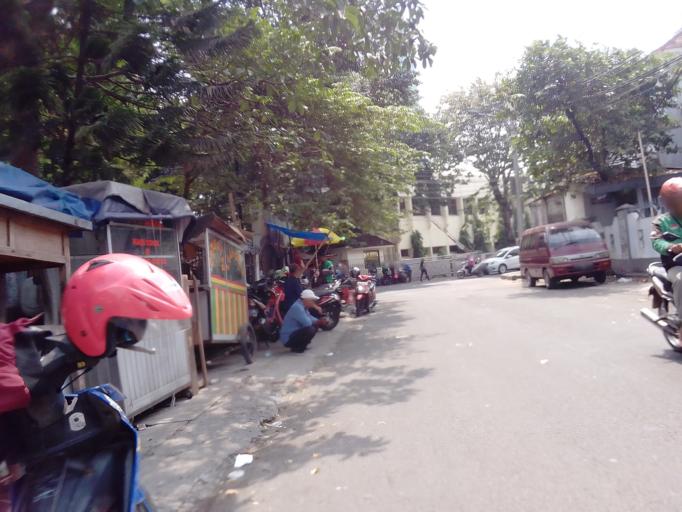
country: ID
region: Jakarta Raya
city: Jakarta
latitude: -6.1825
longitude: 106.8122
